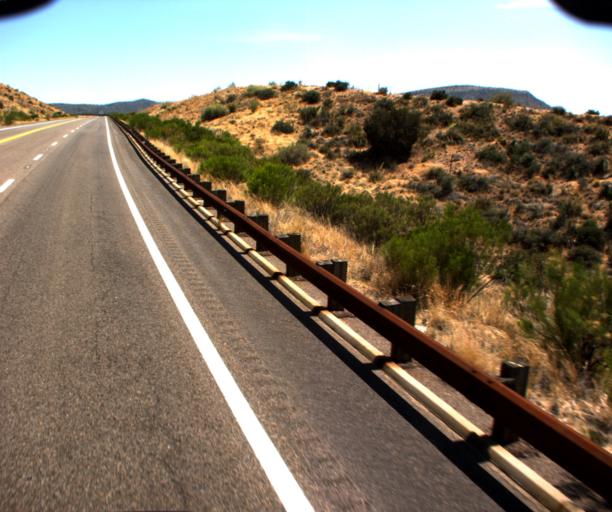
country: US
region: Arizona
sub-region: Gila County
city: Miami
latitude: 33.5563
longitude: -110.9489
